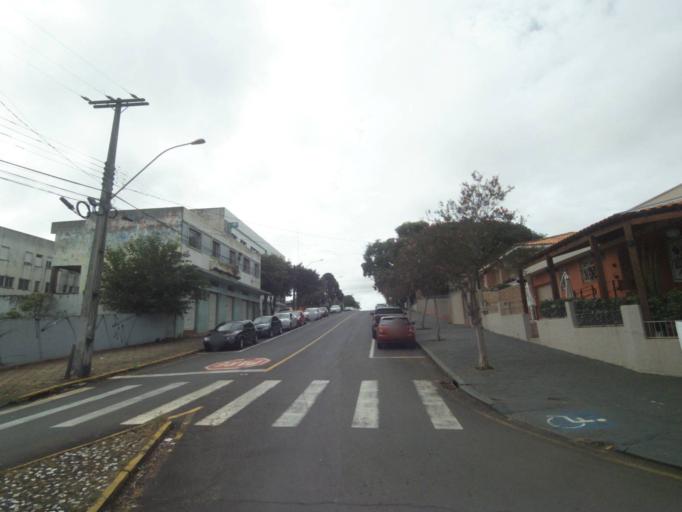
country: BR
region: Parana
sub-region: Telemaco Borba
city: Telemaco Borba
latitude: -24.3288
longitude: -50.6230
